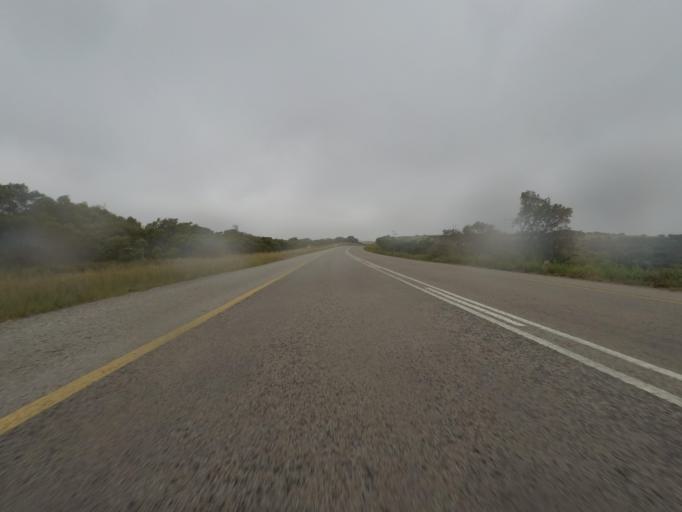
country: ZA
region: Eastern Cape
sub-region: Cacadu District Municipality
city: Grahamstown
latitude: -33.6425
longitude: 26.3667
